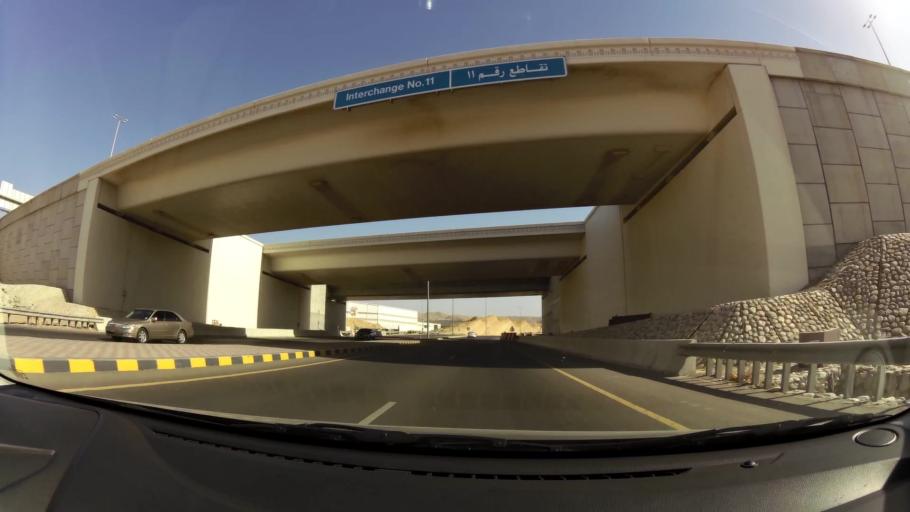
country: OM
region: Muhafazat Masqat
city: As Sib al Jadidah
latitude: 23.5642
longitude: 58.2063
